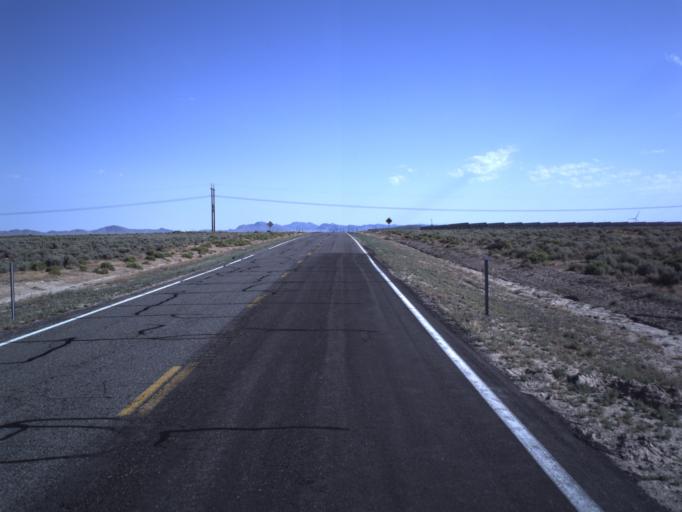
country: US
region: Utah
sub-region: Beaver County
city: Milford
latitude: 38.4832
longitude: -112.9911
